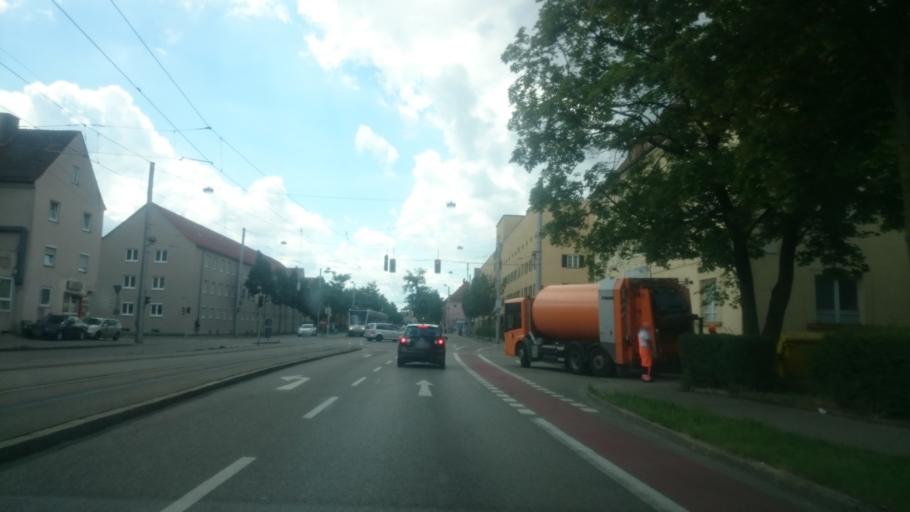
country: DE
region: Bavaria
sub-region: Swabia
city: Augsburg
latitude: 48.3942
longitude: 10.8817
